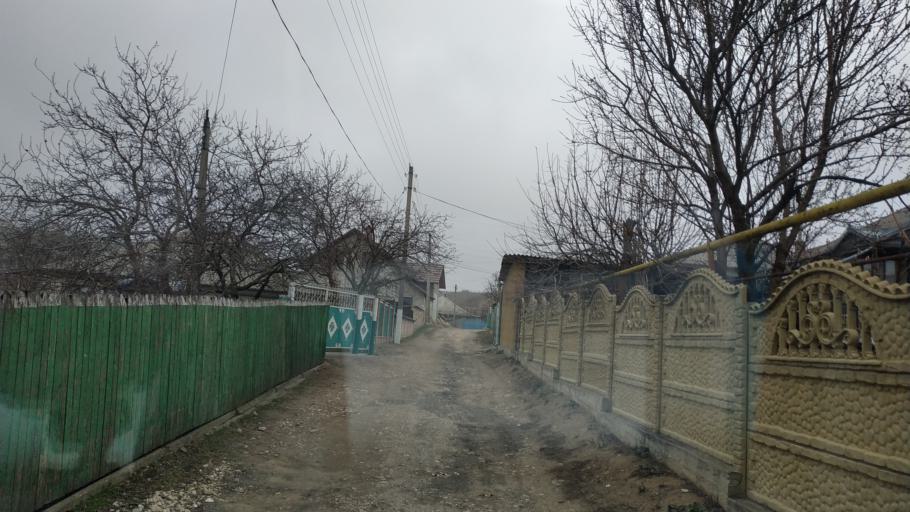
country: MD
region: Hincesti
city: Hincesti
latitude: 46.9076
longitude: 28.6660
